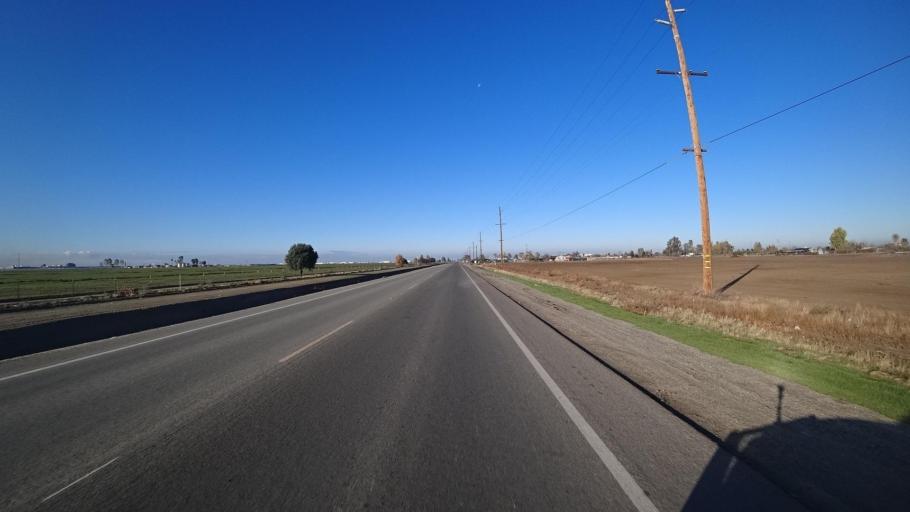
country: US
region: California
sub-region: Kern County
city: Delano
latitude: 35.7755
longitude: -119.2972
